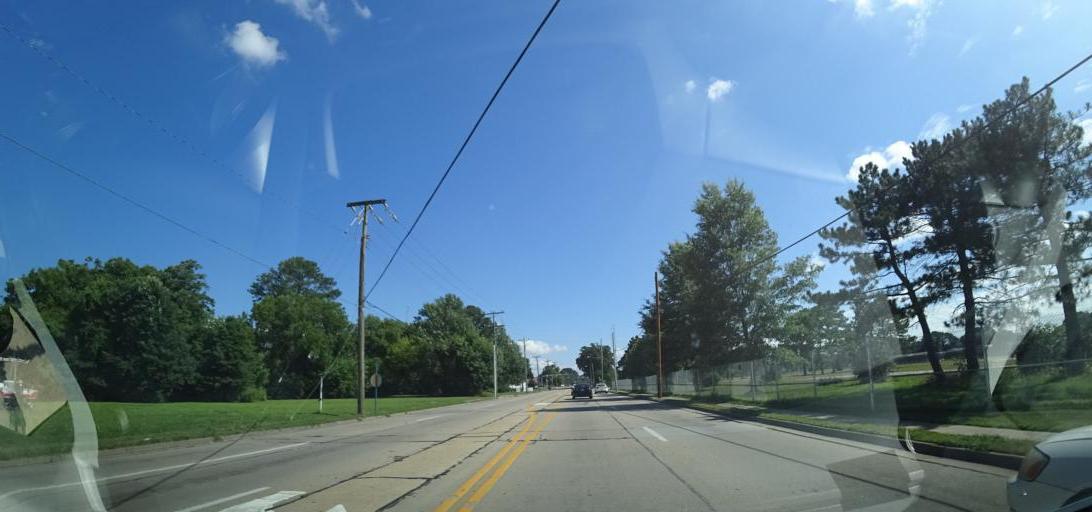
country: US
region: Virginia
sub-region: City of Hampton
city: Hampton
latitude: 37.0299
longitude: -76.3630
